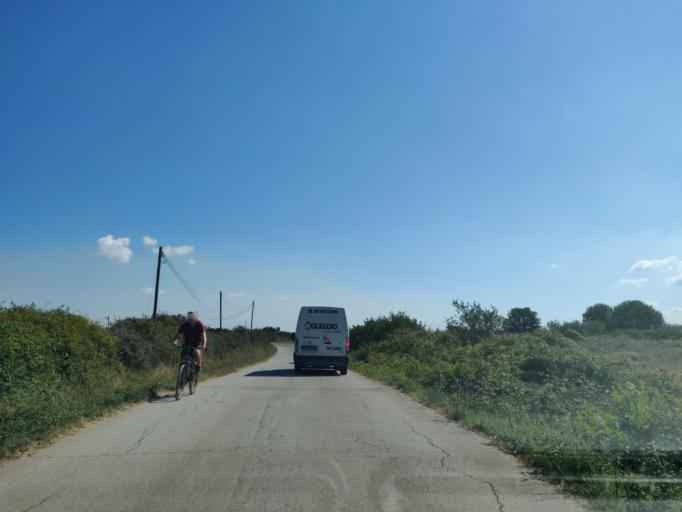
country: IT
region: Latium
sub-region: Citta metropolitana di Roma Capitale
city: Aurelia
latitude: 42.1668
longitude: 11.7431
